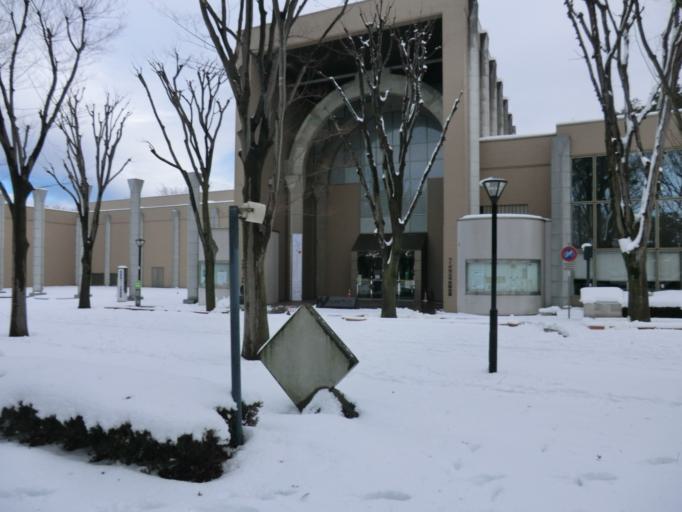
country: JP
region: Ibaraki
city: Naka
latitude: 36.0843
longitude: 140.1119
